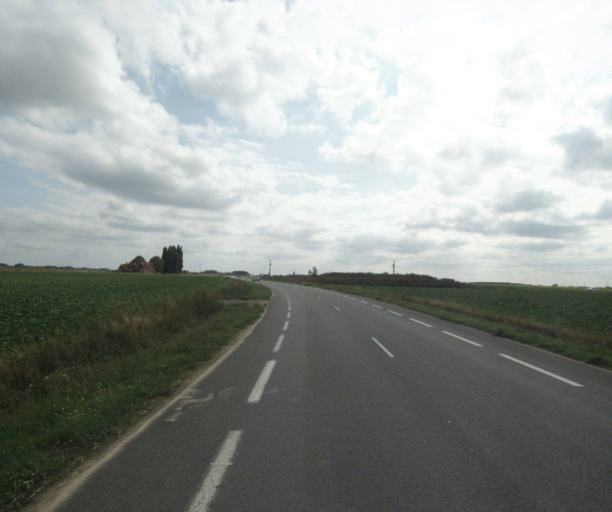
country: FR
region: Nord-Pas-de-Calais
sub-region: Departement du Nord
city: Gruson
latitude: 50.5927
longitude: 3.2288
